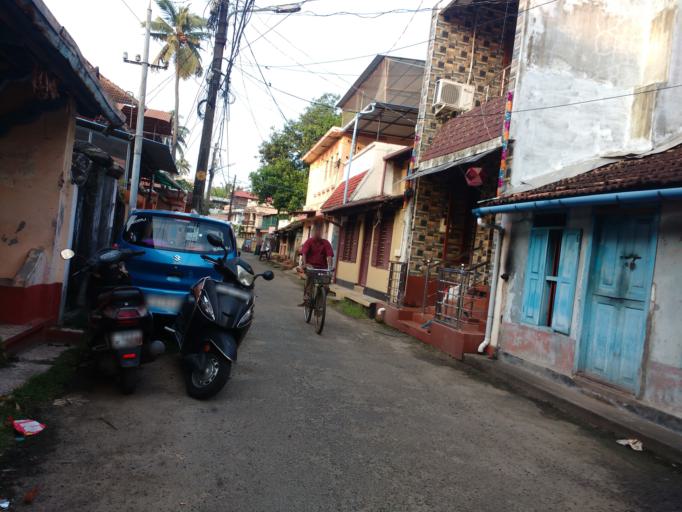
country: IN
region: Kerala
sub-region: Ernakulam
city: Cochin
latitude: 9.9586
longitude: 76.2502
